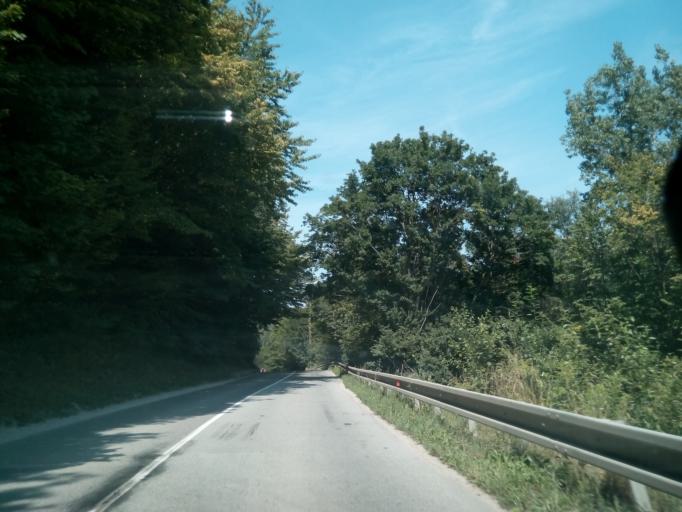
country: SK
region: Kosicky
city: Kosice
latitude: 48.7620
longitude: 21.2458
